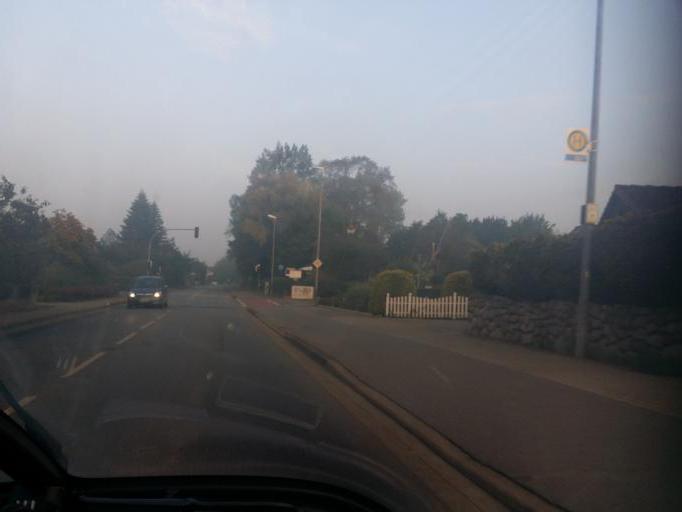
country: DE
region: Schleswig-Holstein
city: Husum
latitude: 54.4883
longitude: 9.0401
